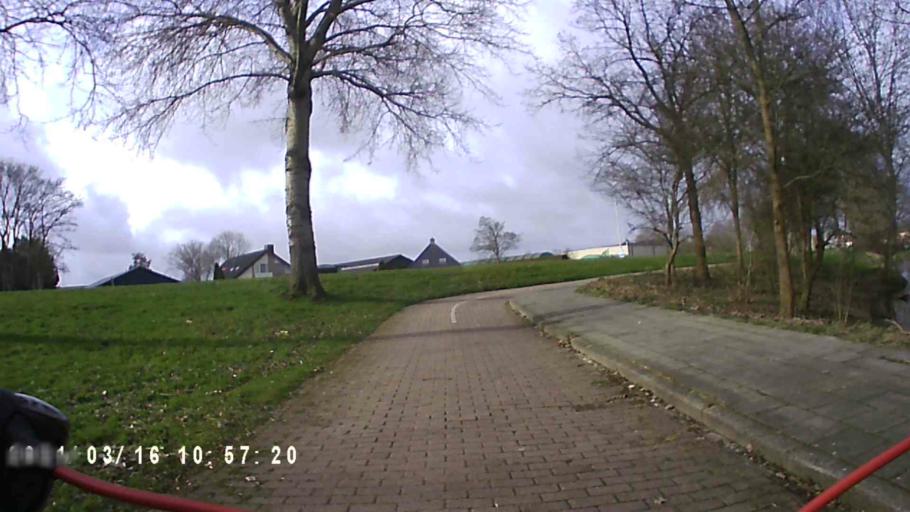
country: NL
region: Friesland
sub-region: Gemeente Dongeradeel
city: Dokkum
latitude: 53.3259
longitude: 6.0083
